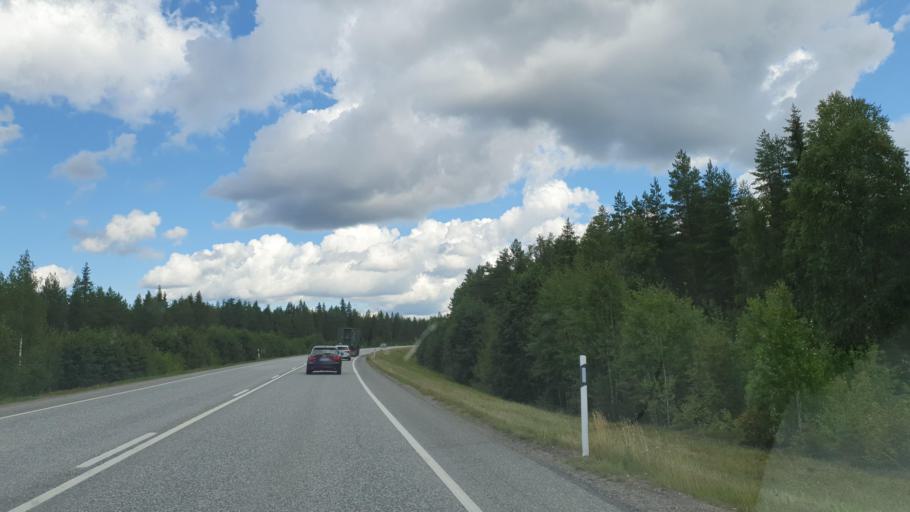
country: FI
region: Kainuu
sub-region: Kajaani
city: Kajaani
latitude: 64.1887
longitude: 27.6024
